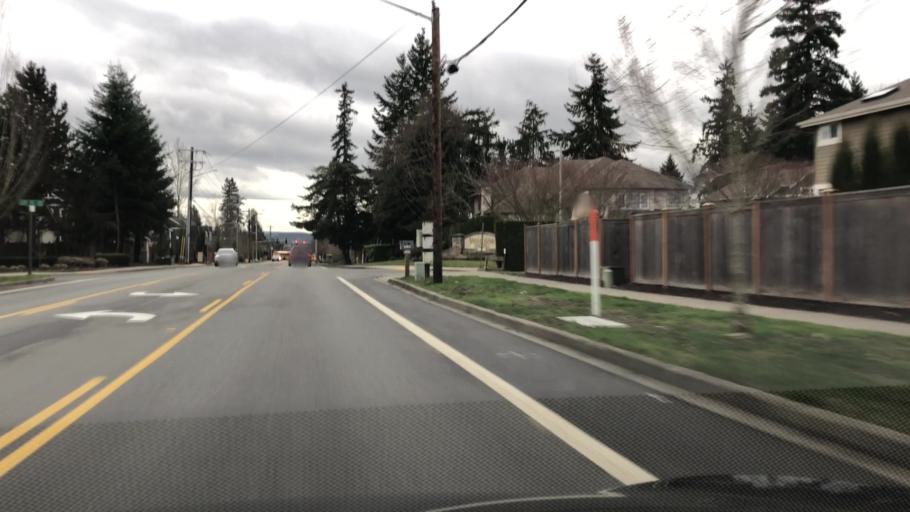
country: US
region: Washington
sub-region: Snohomish County
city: North Creek
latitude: 47.8081
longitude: -122.1808
